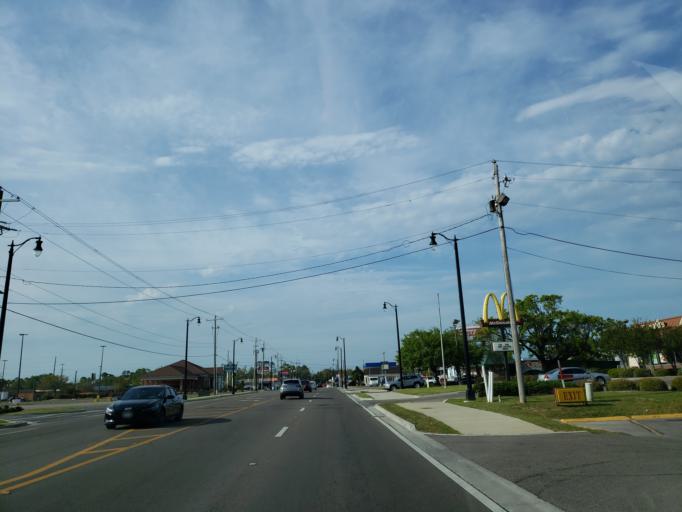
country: US
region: Mississippi
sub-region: Harrison County
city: West Gulfport
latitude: 30.3906
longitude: -89.0442
